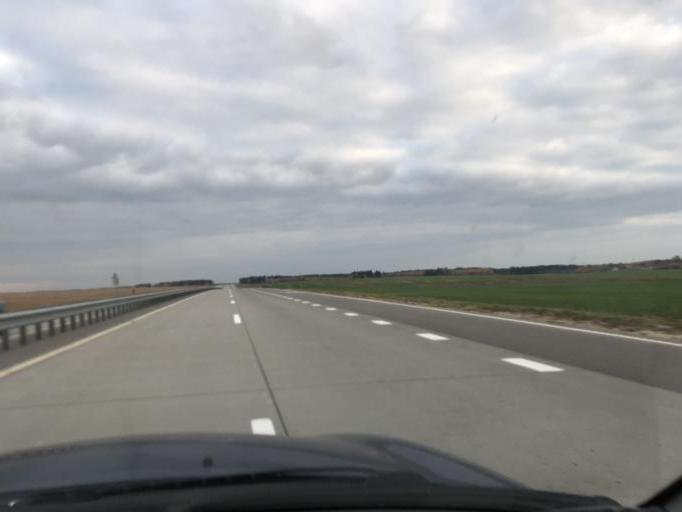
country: BY
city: Fanipol
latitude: 53.8101
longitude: 27.2877
